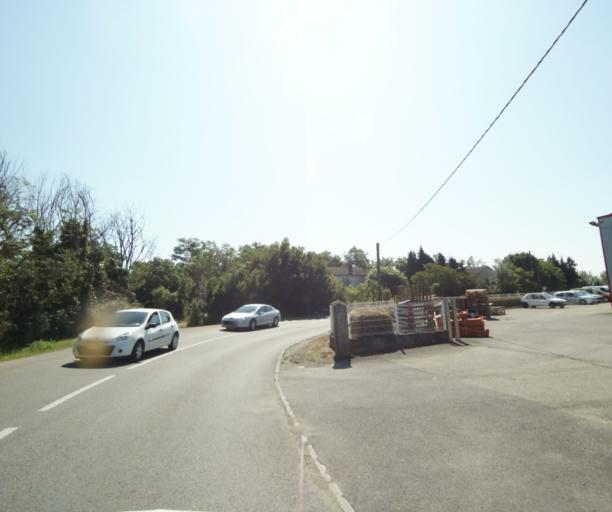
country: FR
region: Midi-Pyrenees
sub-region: Departement du Tarn-et-Garonne
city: Montbeton
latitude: 44.0198
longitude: 1.3230
